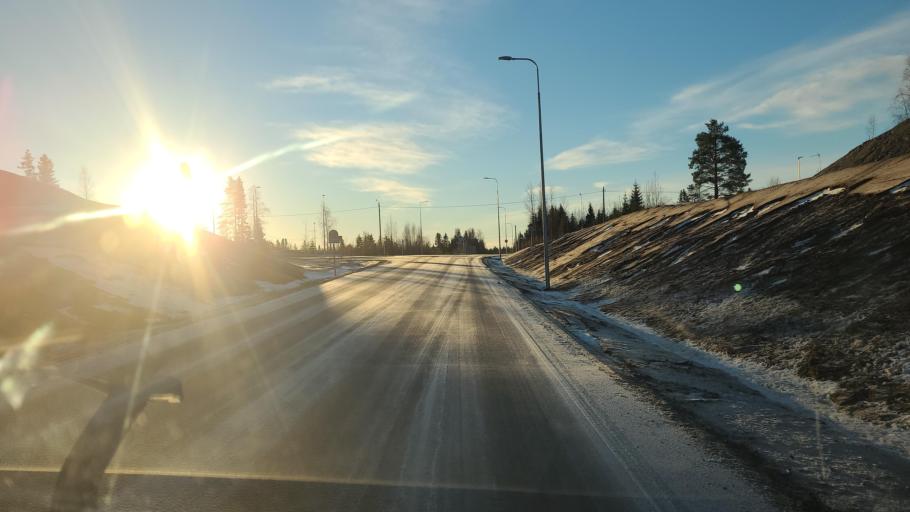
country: FI
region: Lapland
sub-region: Kemi-Tornio
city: Kemi
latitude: 65.6783
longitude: 24.7440
